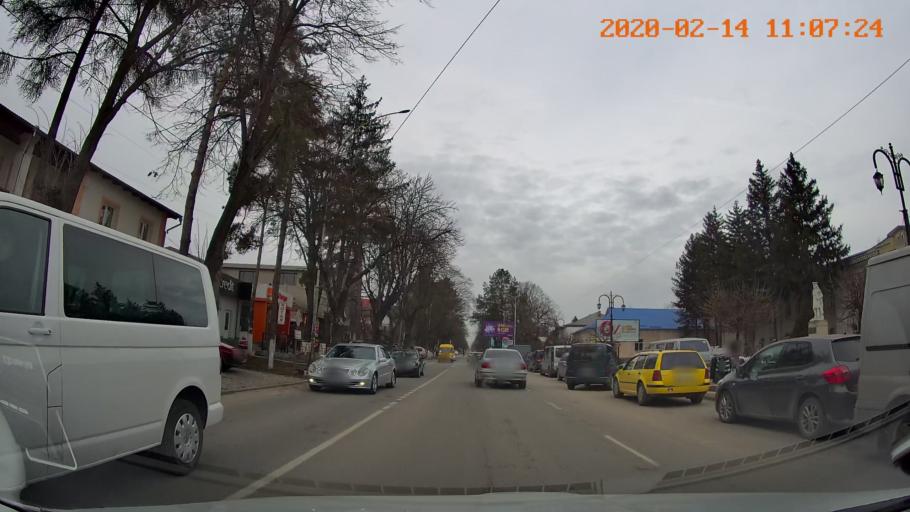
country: MD
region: Raionul Edinet
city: Edinet
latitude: 48.1693
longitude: 27.3063
